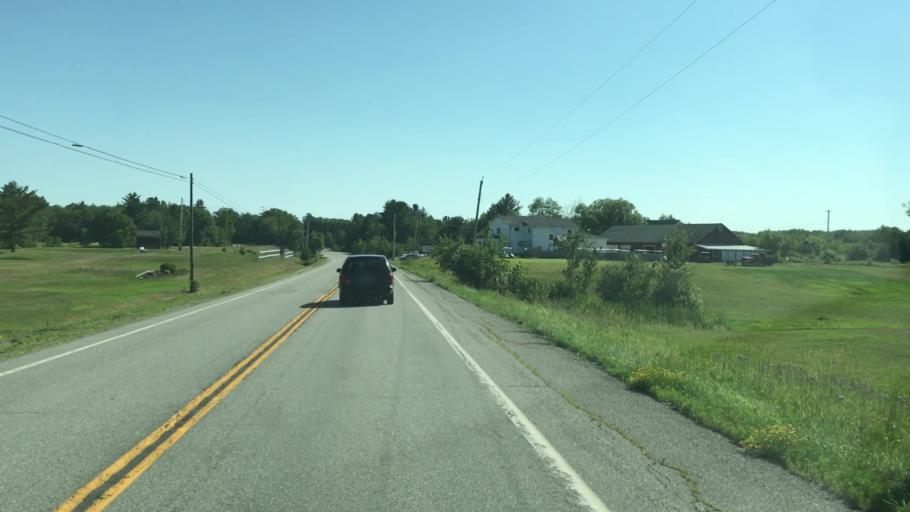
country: US
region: Maine
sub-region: Penobscot County
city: Enfield
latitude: 45.2985
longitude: -68.6187
